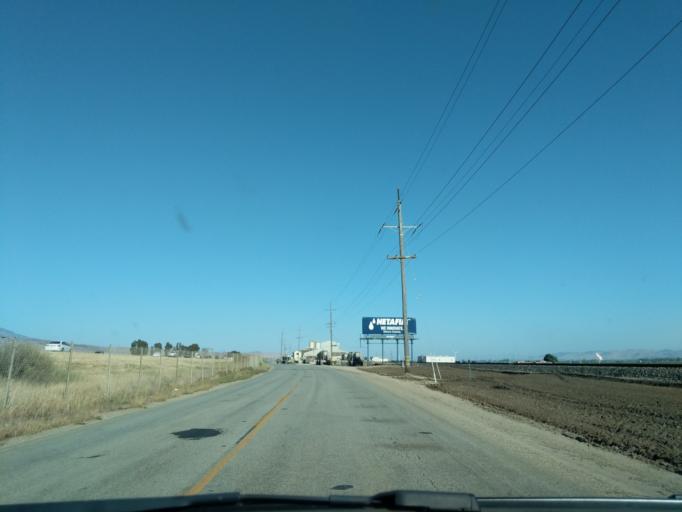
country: US
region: California
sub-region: Monterey County
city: Soledad
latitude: 36.4571
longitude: -121.3765
